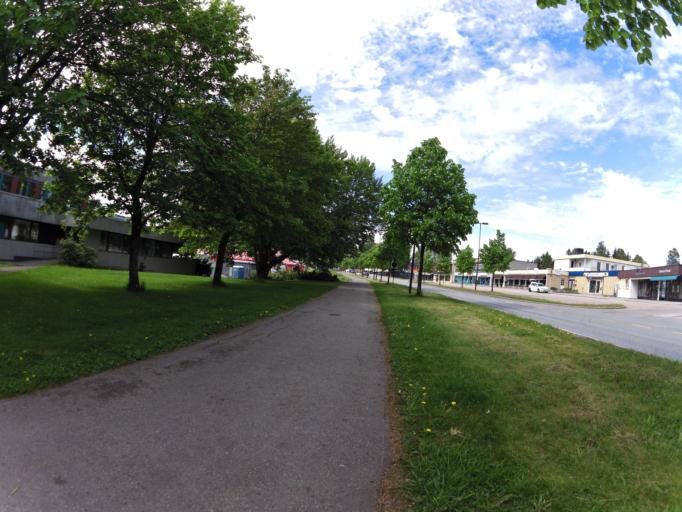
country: NO
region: Ostfold
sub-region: Rade
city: Karlshus
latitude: 59.3522
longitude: 10.8715
